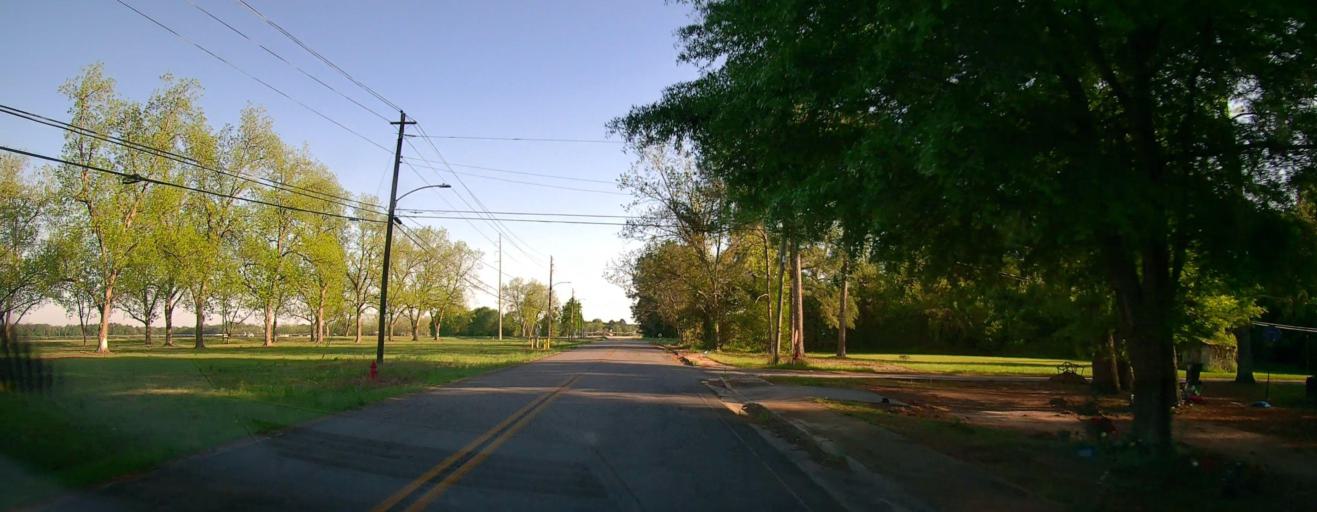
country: US
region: Georgia
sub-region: Macon County
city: Oglethorpe
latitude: 32.2883
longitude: -84.0578
